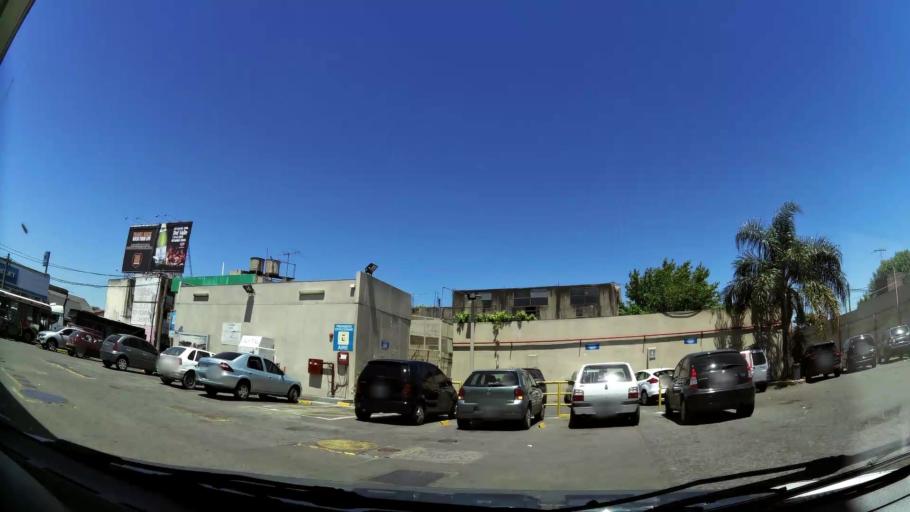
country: AR
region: Buenos Aires
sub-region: Partido de San Isidro
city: San Isidro
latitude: -34.4974
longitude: -58.5557
